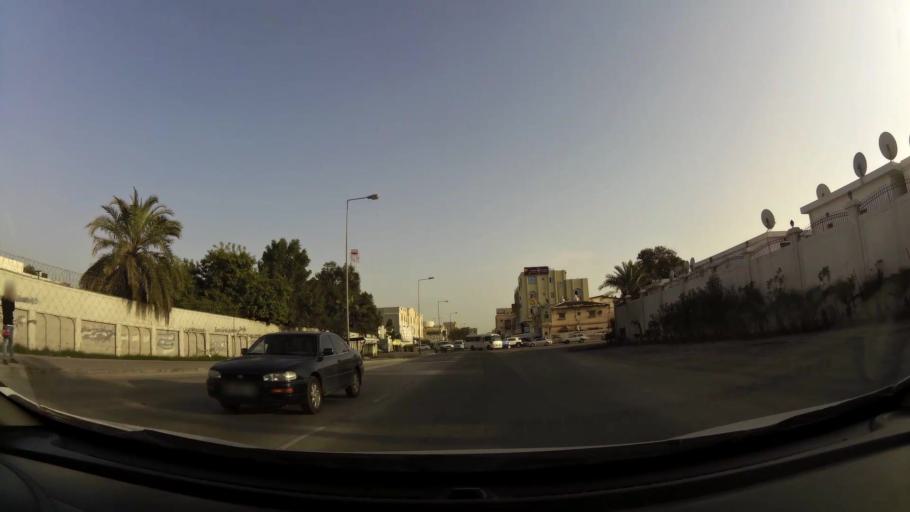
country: BH
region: Manama
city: Jidd Hafs
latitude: 26.1973
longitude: 50.4858
